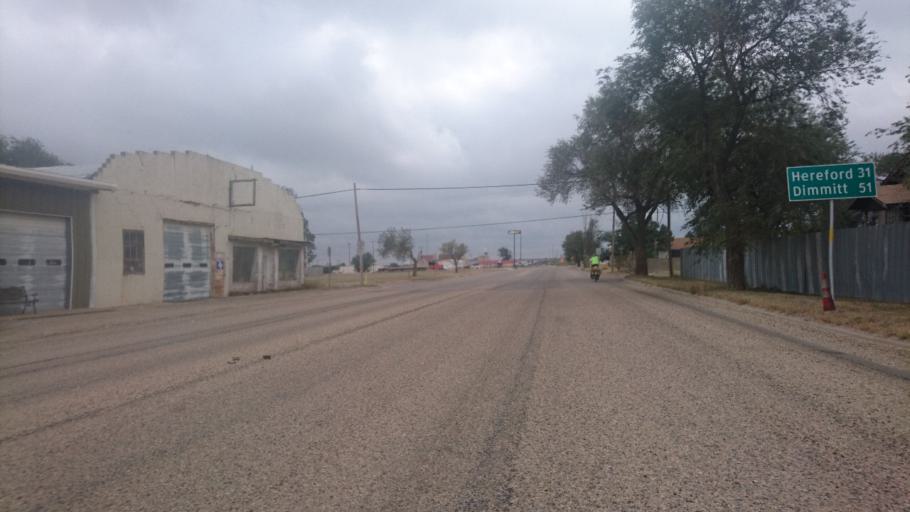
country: US
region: Texas
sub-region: Oldham County
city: Vega
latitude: 35.2424
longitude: -102.4285
